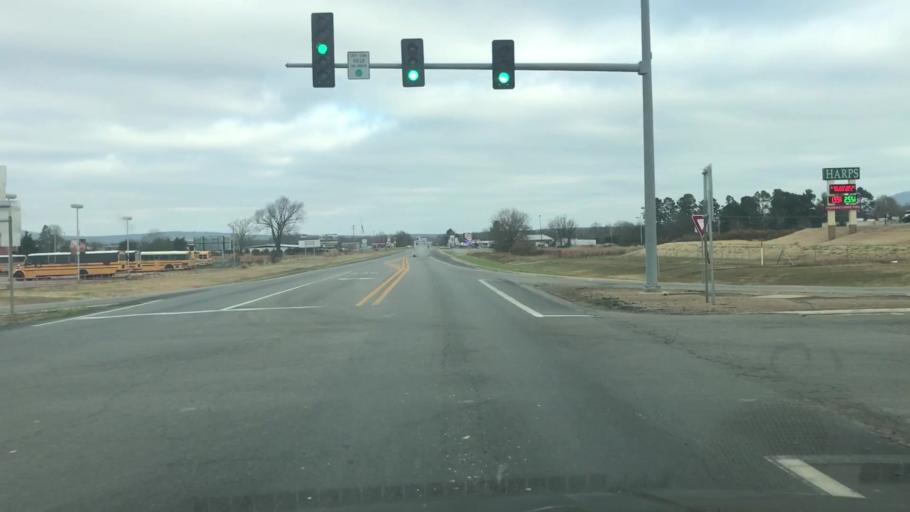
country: US
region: Arkansas
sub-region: Scott County
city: Waldron
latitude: 34.8968
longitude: -94.1075
